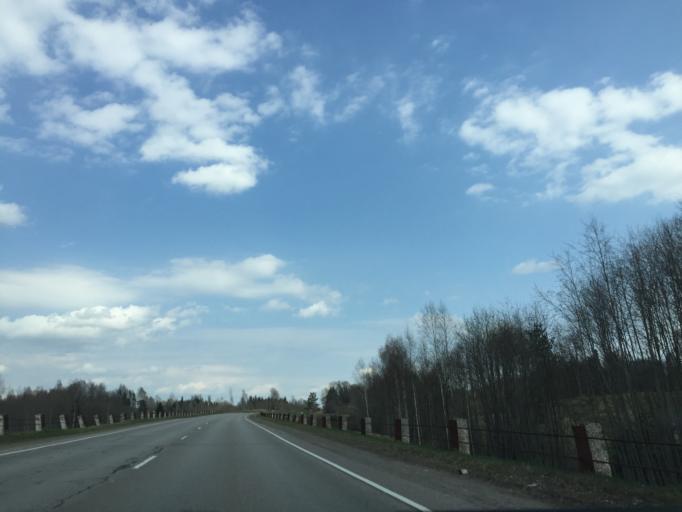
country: LV
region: Apes Novads
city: Ape
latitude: 57.5537
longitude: 26.8942
